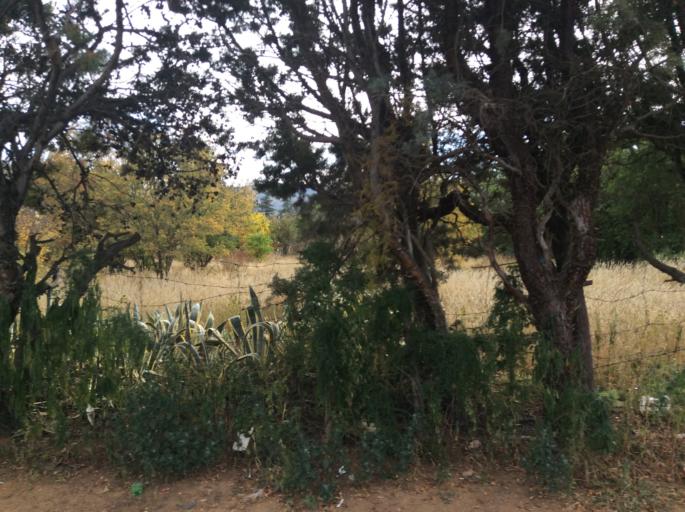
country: LS
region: Mafeteng
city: Mafeteng
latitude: -29.7312
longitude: 27.0320
